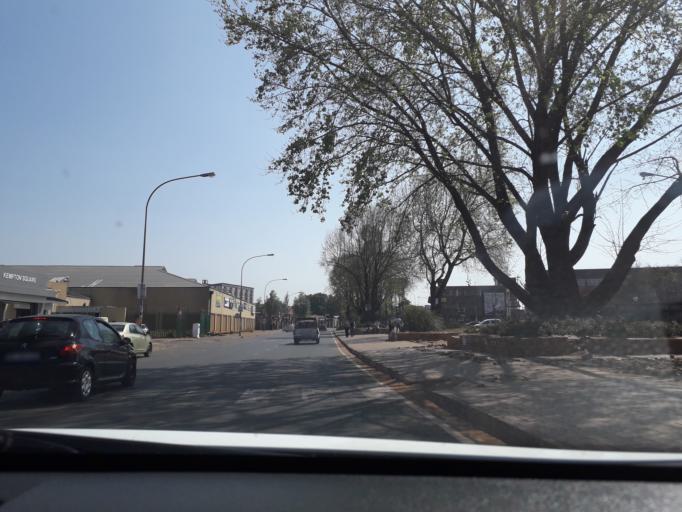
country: ZA
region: Gauteng
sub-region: City of Johannesburg Metropolitan Municipality
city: Modderfontein
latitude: -26.1068
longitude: 28.2317
